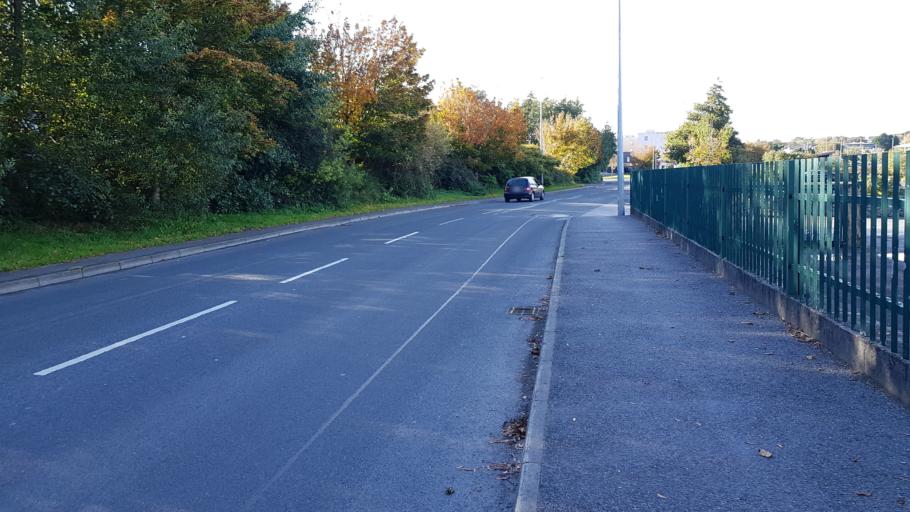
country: IE
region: Connaught
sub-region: County Galway
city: Gaillimh
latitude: 53.2843
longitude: -9.0413
